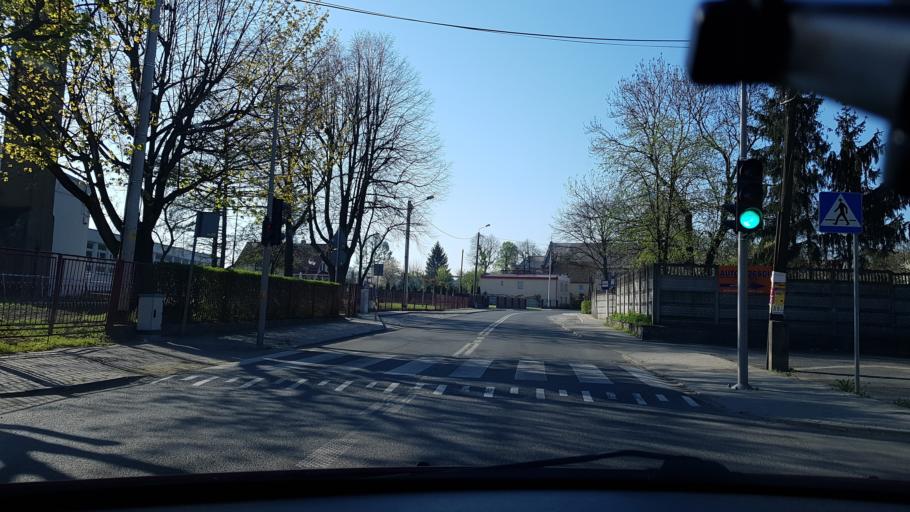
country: PL
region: Opole Voivodeship
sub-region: Powiat nyski
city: Nysa
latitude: 50.4345
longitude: 17.3055
